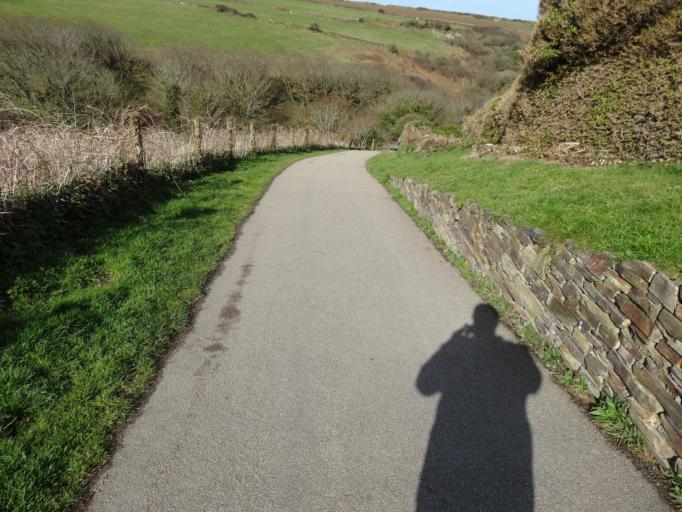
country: GB
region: England
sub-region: Cornwall
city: Tintagel
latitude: 50.6642
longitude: -4.7540
